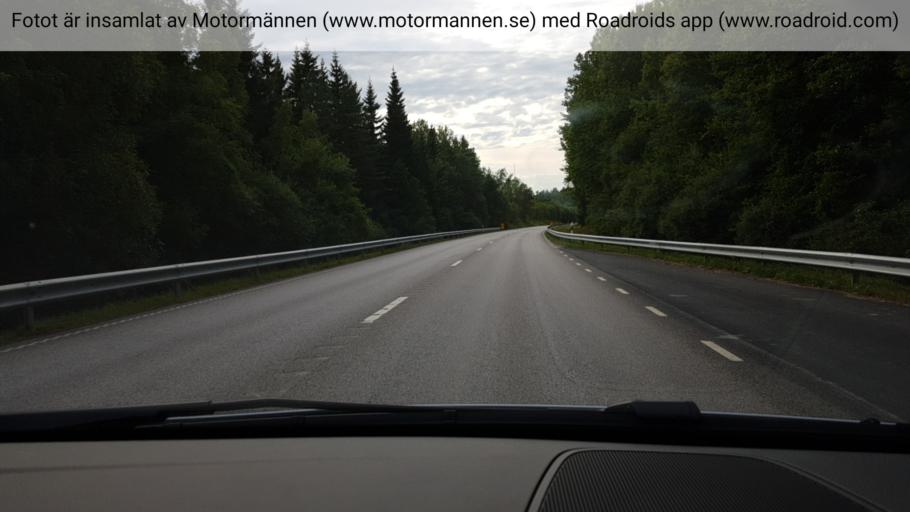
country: SE
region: Stockholm
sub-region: Norrtalje Kommun
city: Skanninge
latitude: 59.8933
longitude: 18.6288
